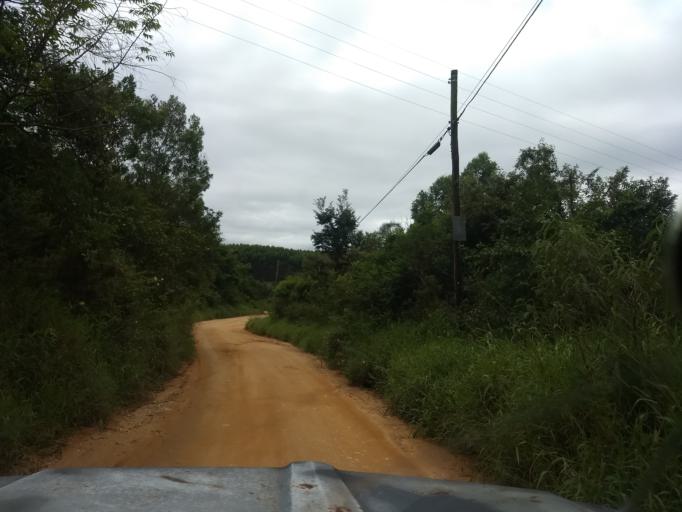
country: BR
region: Sao Paulo
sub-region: Cabreuva
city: Cabreuva
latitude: -23.3930
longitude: -47.1949
